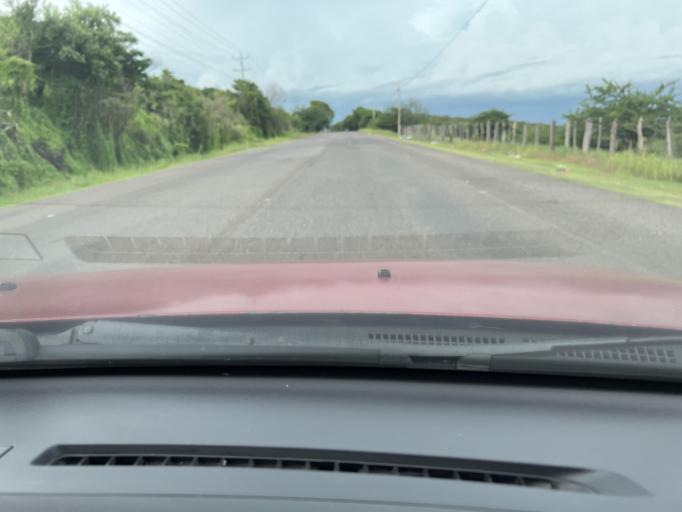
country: SV
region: La Union
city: San Alejo
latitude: 13.4015
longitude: -87.8959
